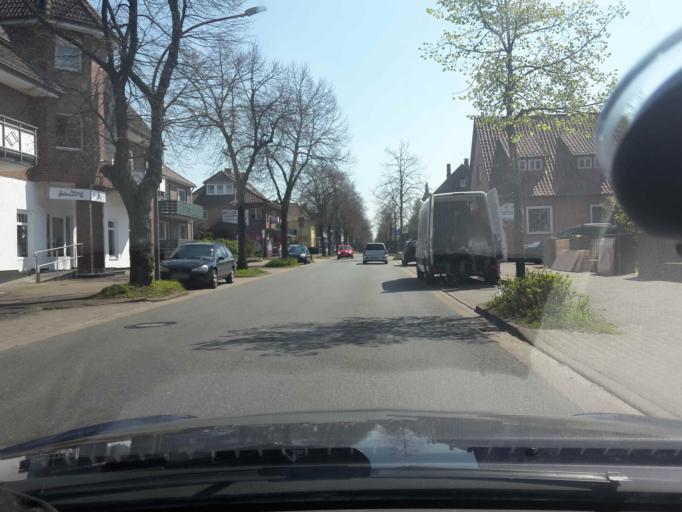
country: DE
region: Lower Saxony
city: Schneverdingen
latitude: 53.1142
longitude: 9.7926
